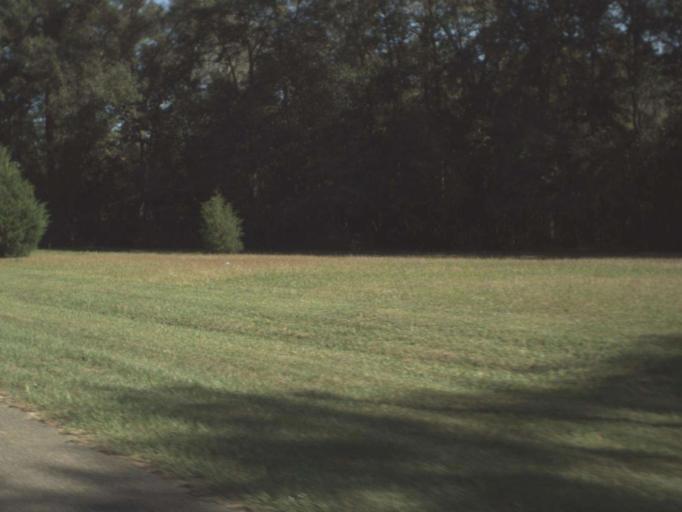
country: US
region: Florida
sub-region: Walton County
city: DeFuniak Springs
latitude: 30.6577
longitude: -85.9365
